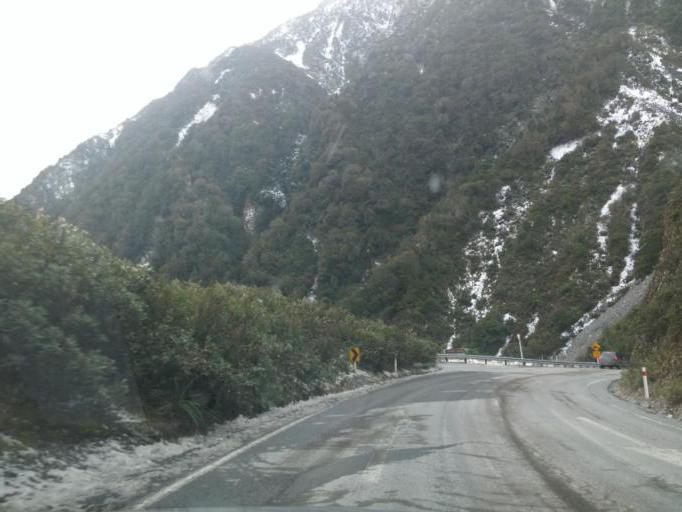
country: NZ
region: West Coast
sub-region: Grey District
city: Greymouth
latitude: -42.8813
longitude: 171.5551
